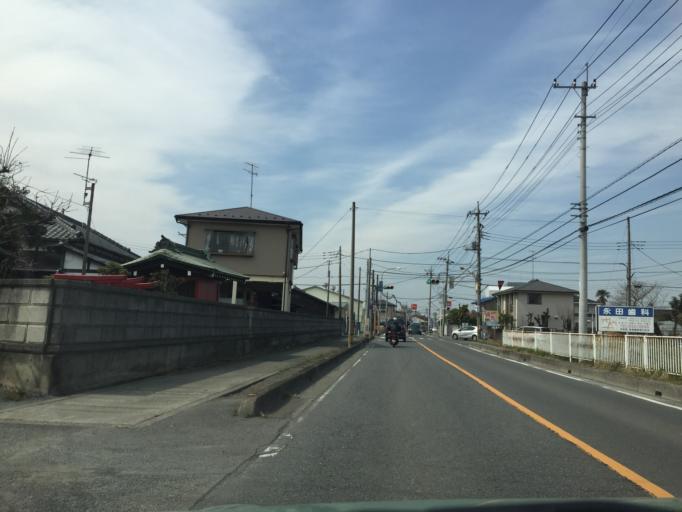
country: JP
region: Saitama
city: Yono
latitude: 35.8849
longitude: 139.5940
